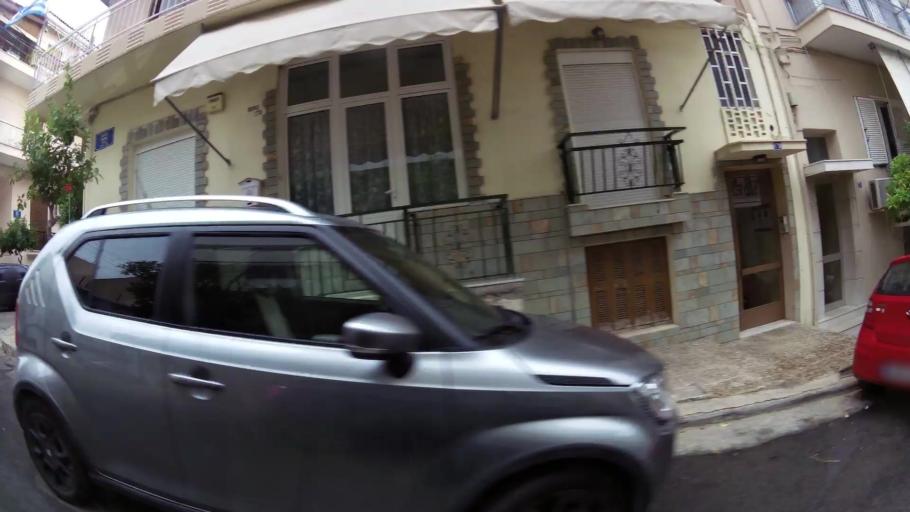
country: GR
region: Attica
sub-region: Nomos Piraios
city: Korydallos
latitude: 37.9867
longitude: 23.6501
